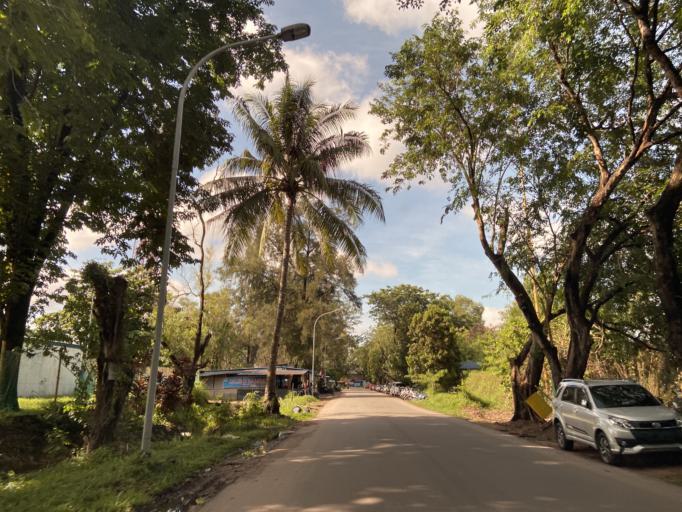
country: SG
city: Singapore
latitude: 1.1709
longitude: 104.0073
